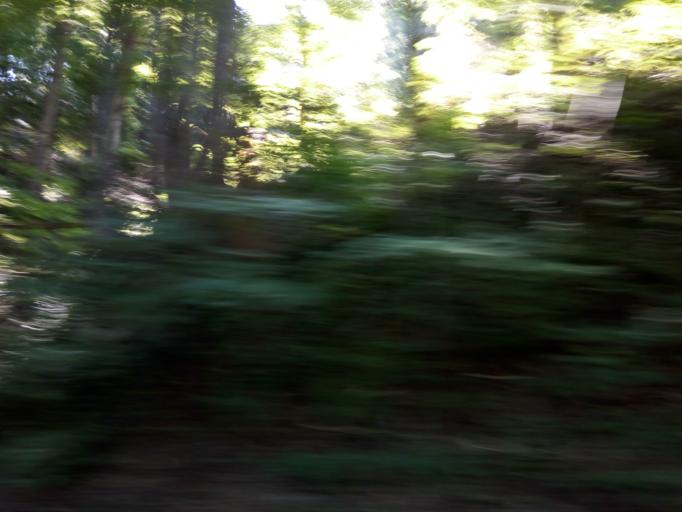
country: US
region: Tennessee
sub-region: Sevier County
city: Gatlinburg
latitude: 35.7049
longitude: -83.5541
